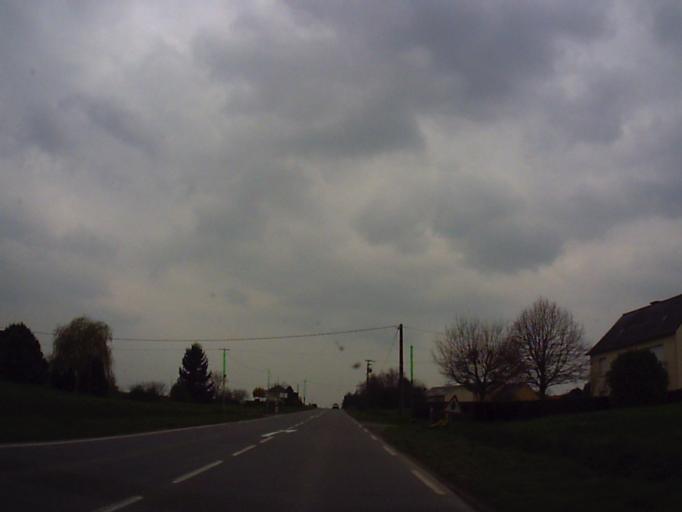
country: FR
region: Brittany
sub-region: Departement d'Ille-et-Vilaine
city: Saint-Gilles
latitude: 48.1303
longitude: -1.8359
